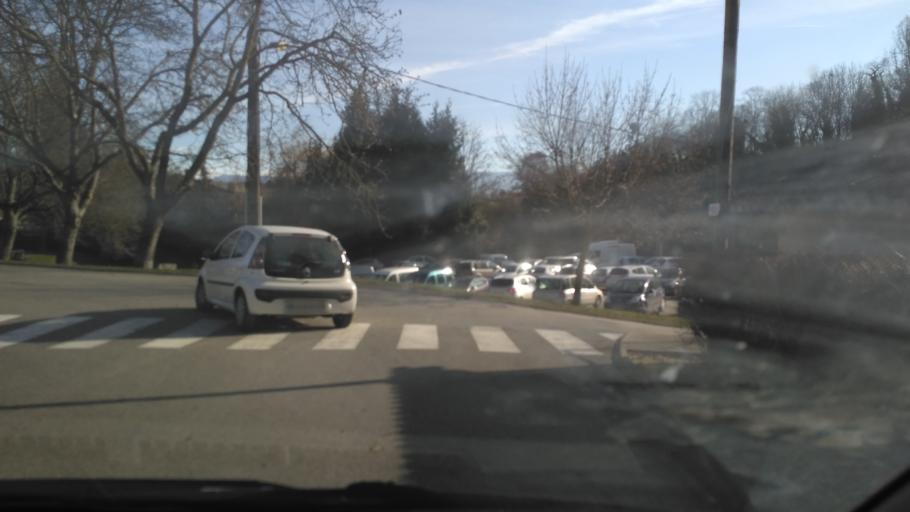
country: FR
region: Rhone-Alpes
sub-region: Departement de l'Isere
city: Saint-Antoine-l'Abbaye
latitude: 45.1732
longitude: 5.2177
